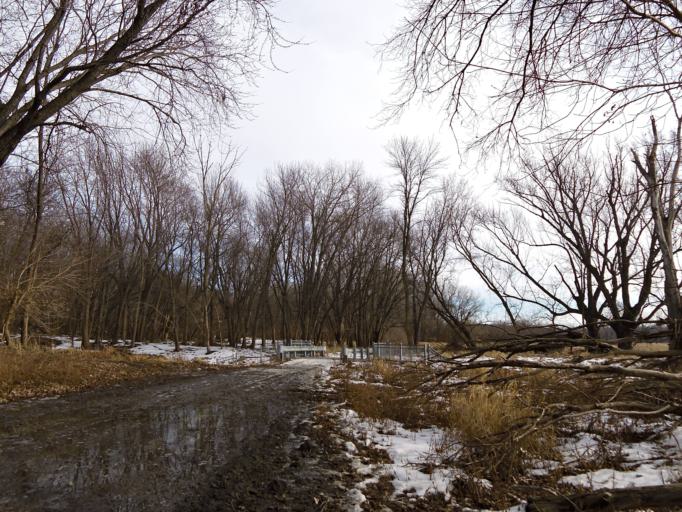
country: US
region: Minnesota
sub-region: Dakota County
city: Eagan
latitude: 44.8551
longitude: -93.2092
